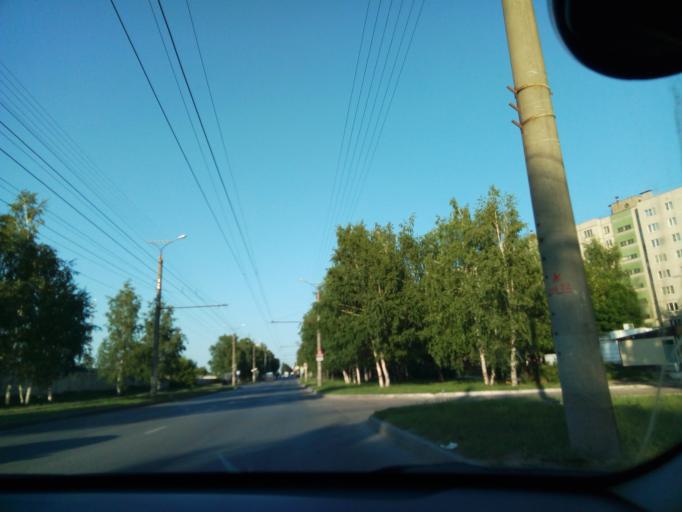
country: RU
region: Chuvashia
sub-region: Cheboksarskiy Rayon
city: Cheboksary
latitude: 56.1087
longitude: 47.2995
